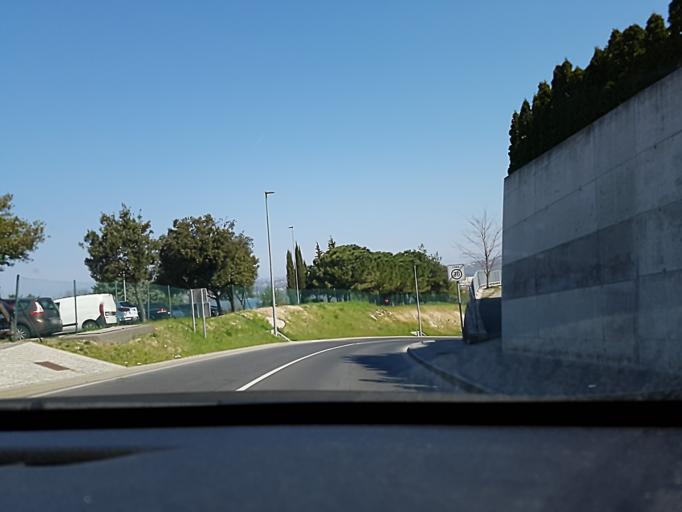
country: SI
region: Koper-Capodistria
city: Koper
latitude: 45.5430
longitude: 13.7126
